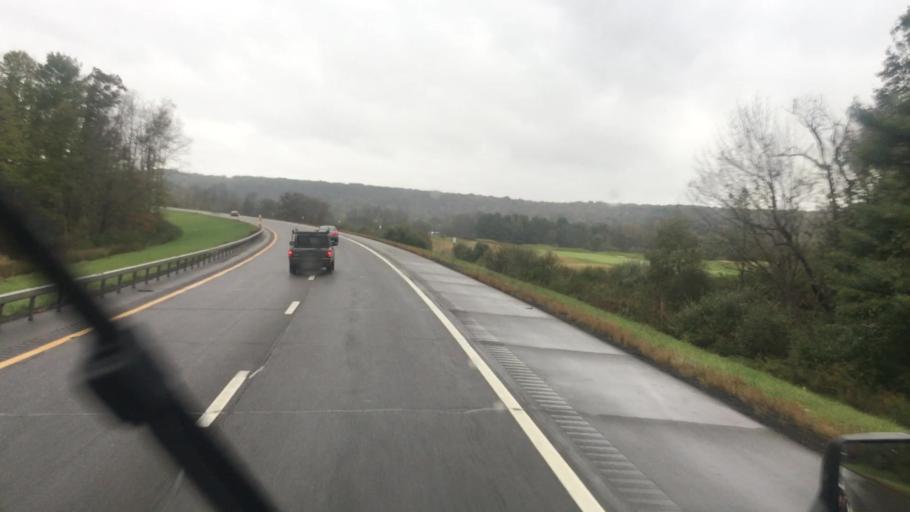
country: US
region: New York
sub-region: Tioga County
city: Apalachin
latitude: 42.0907
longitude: -76.1703
